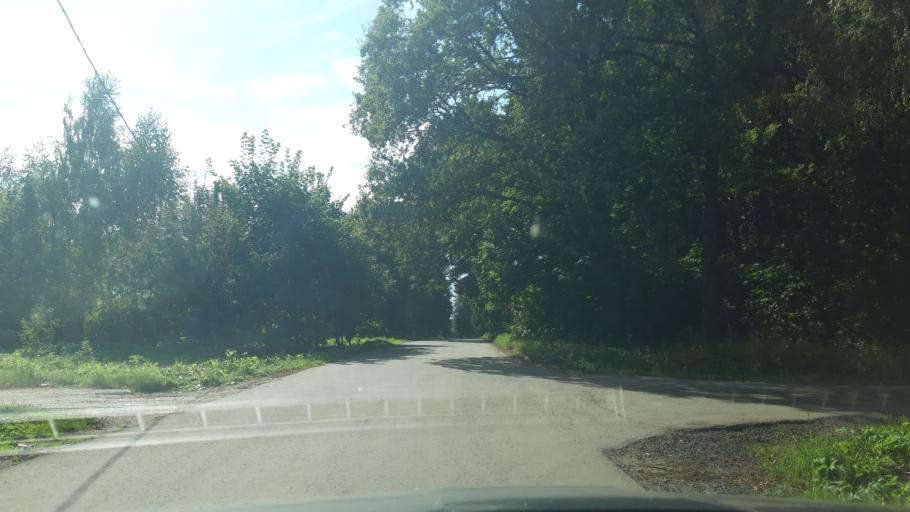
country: RU
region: Moskovskaya
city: Chashnikovo
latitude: 56.0357
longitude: 37.1707
